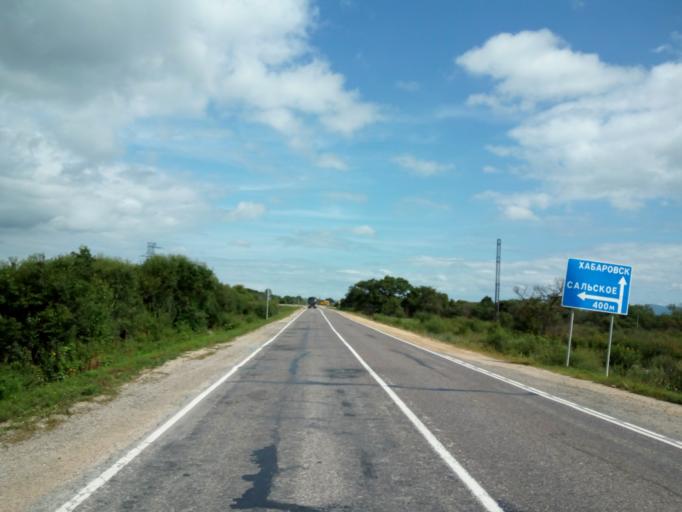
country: RU
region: Primorskiy
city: Dal'nerechensk
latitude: 45.9684
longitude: 133.7844
